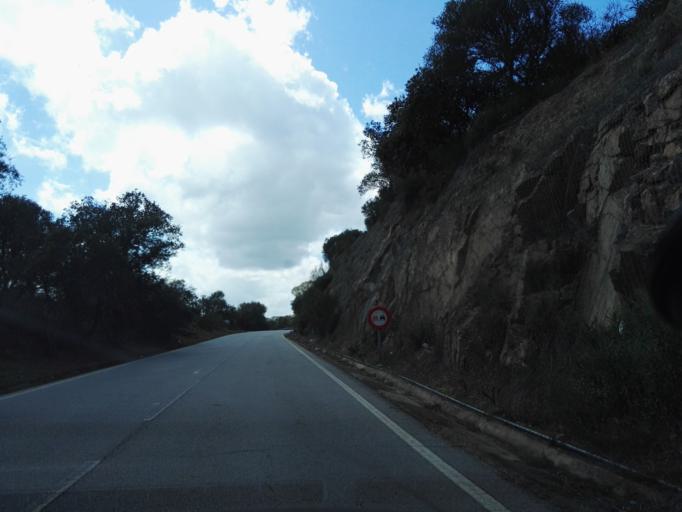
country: PT
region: Portalegre
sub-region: Campo Maior
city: Campo Maior
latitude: 38.9966
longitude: -7.1483
